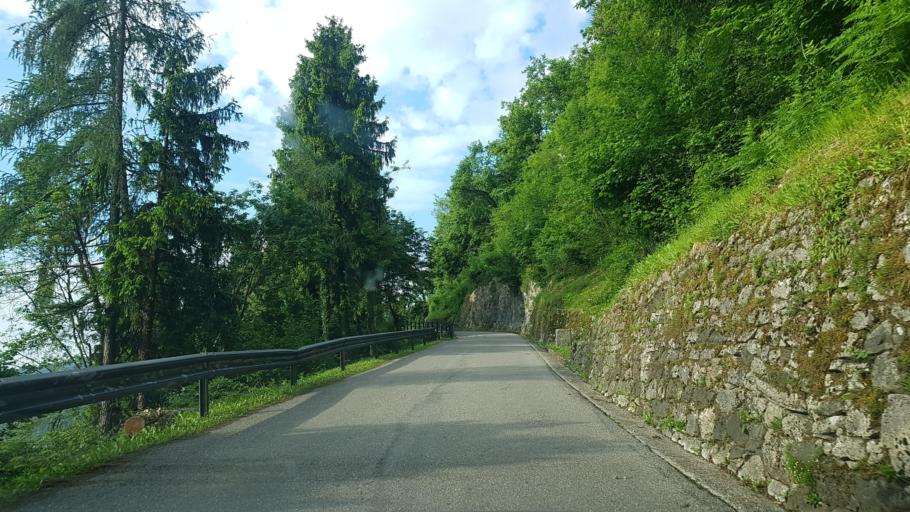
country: IT
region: Friuli Venezia Giulia
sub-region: Provincia di Udine
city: Arta Terme
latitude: 46.4684
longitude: 13.0186
